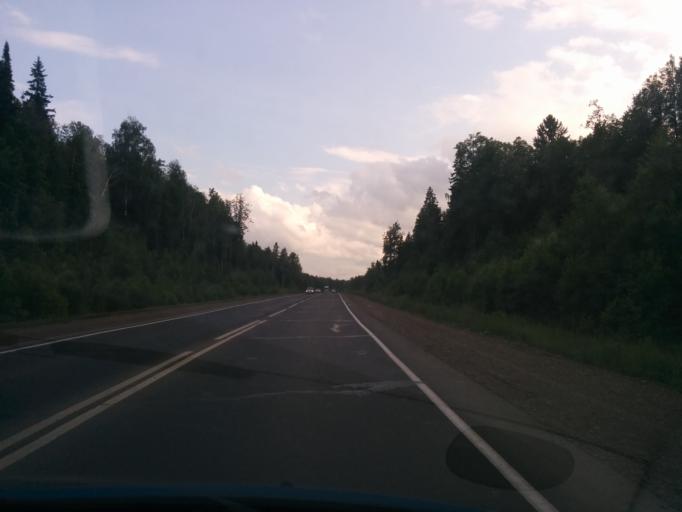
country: RU
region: Perm
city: Novyye Lyady
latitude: 58.0800
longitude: 56.4311
